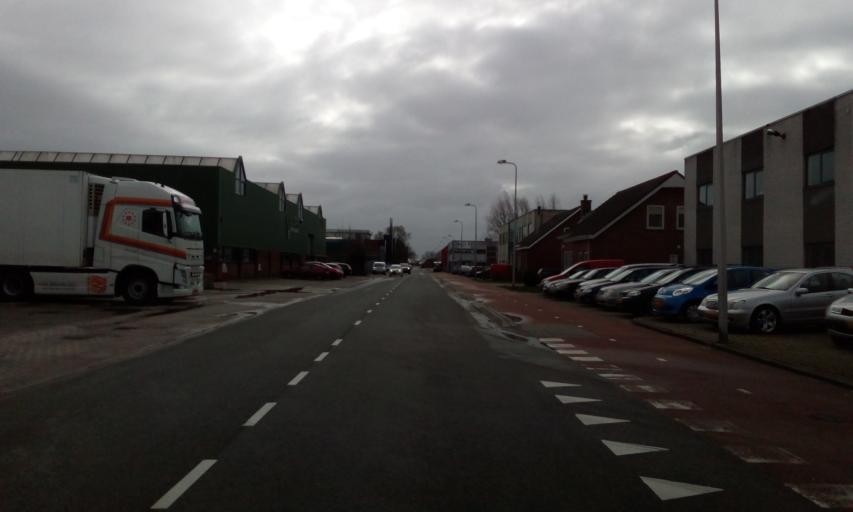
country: NL
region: South Holland
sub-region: Gemeente Kaag en Braassem
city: Leimuiden
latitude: 52.1794
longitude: 4.7122
